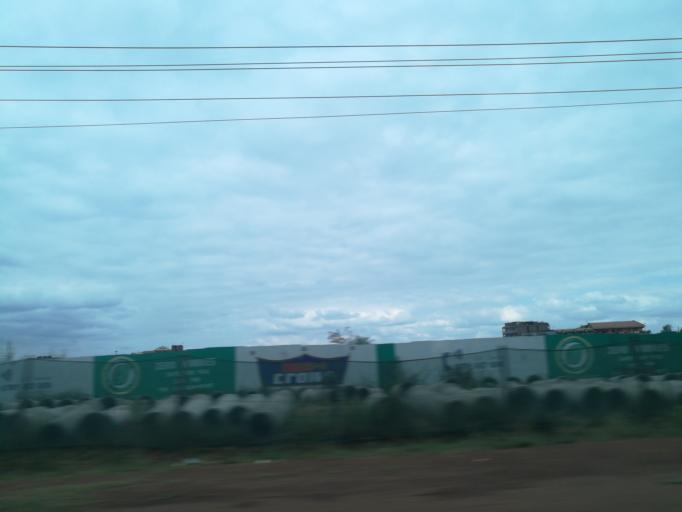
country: KE
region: Nairobi Area
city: Thika
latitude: -1.0721
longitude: 37.0487
